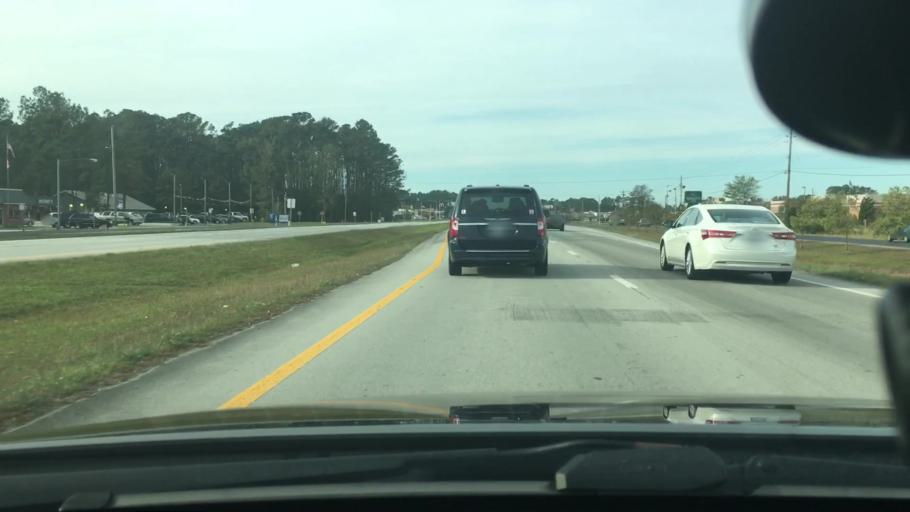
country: US
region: North Carolina
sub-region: Craven County
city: Havelock
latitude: 34.9044
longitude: -76.9327
